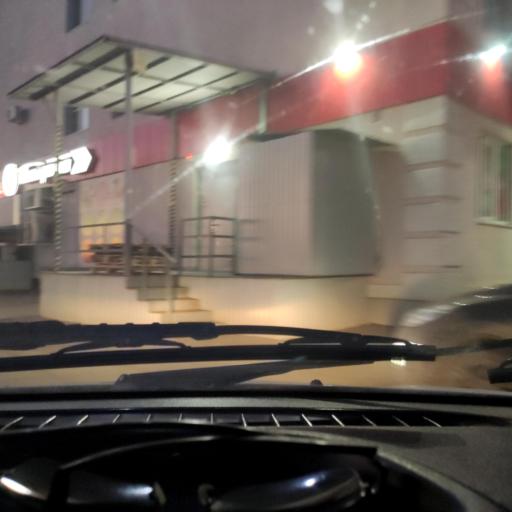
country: RU
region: Samara
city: Podstepki
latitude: 53.5270
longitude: 49.1845
